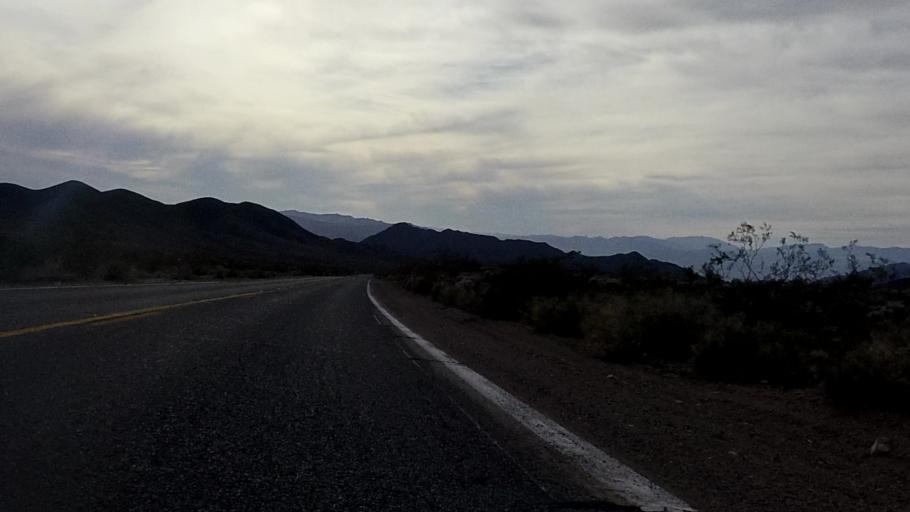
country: US
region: Nevada
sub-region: Nye County
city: Pahrump
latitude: 35.9118
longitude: -116.4482
